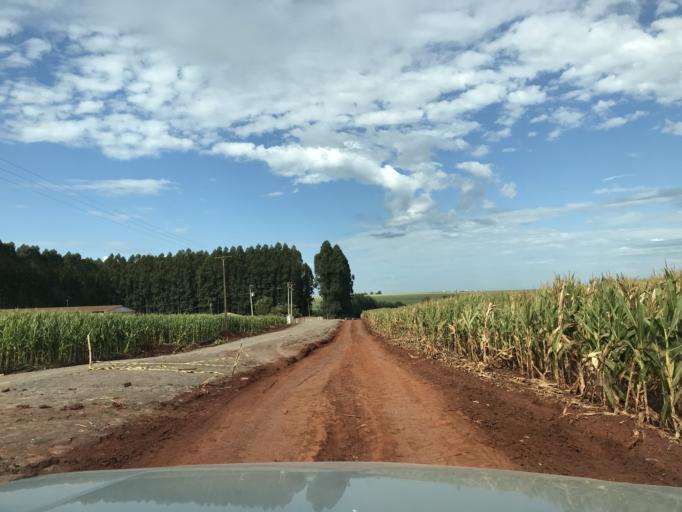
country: BR
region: Parana
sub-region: Palotina
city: Palotina
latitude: -24.2981
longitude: -53.8142
